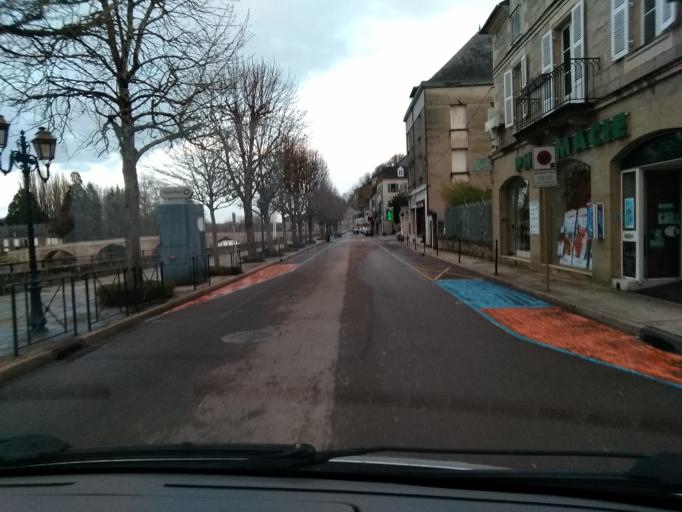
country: FR
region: Aquitaine
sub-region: Departement de la Dordogne
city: Terrasson-Lavilledieu
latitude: 45.1277
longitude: 1.3032
